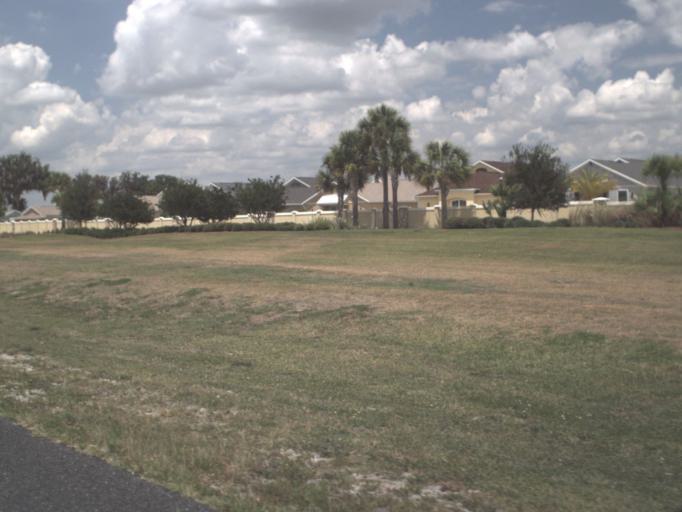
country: US
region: Florida
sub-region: Sumter County
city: Wildwood
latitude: 28.8384
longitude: -82.0133
